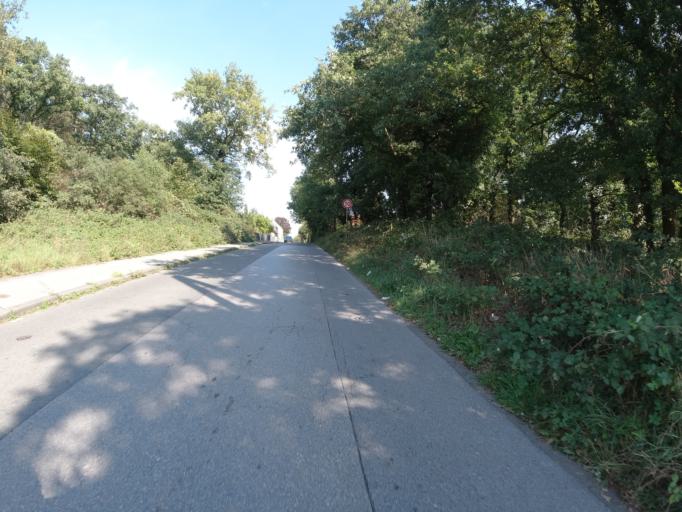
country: DE
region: North Rhine-Westphalia
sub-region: Regierungsbezirk Dusseldorf
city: Moers
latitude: 51.4716
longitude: 6.6698
